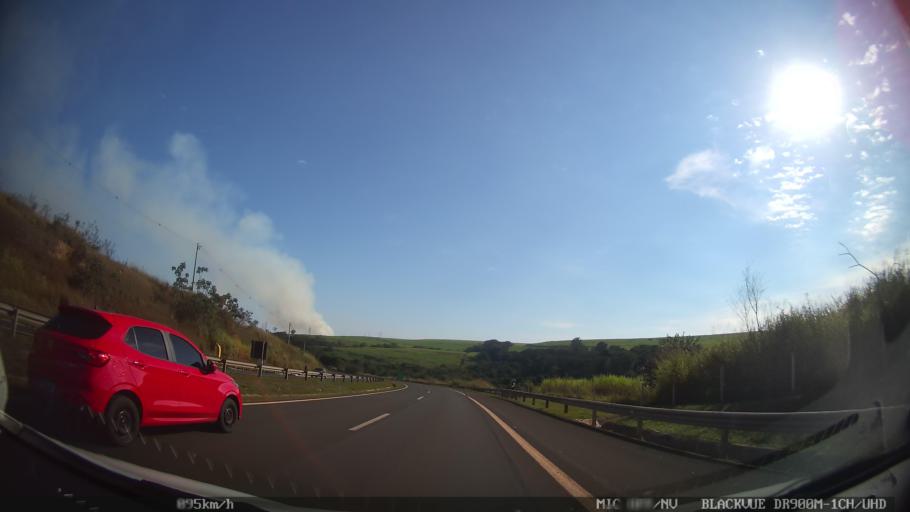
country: BR
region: Sao Paulo
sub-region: Piracicaba
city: Piracicaba
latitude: -22.6826
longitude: -47.5774
